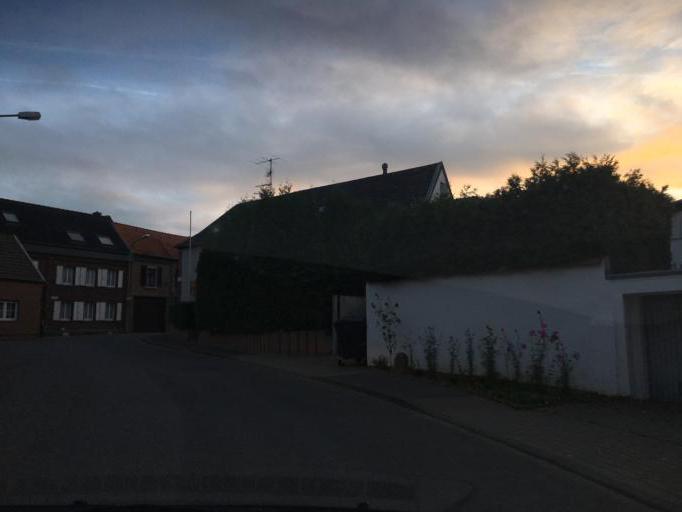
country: DE
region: North Rhine-Westphalia
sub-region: Regierungsbezirk Koln
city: Norvenich
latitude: 50.7628
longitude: 6.6404
